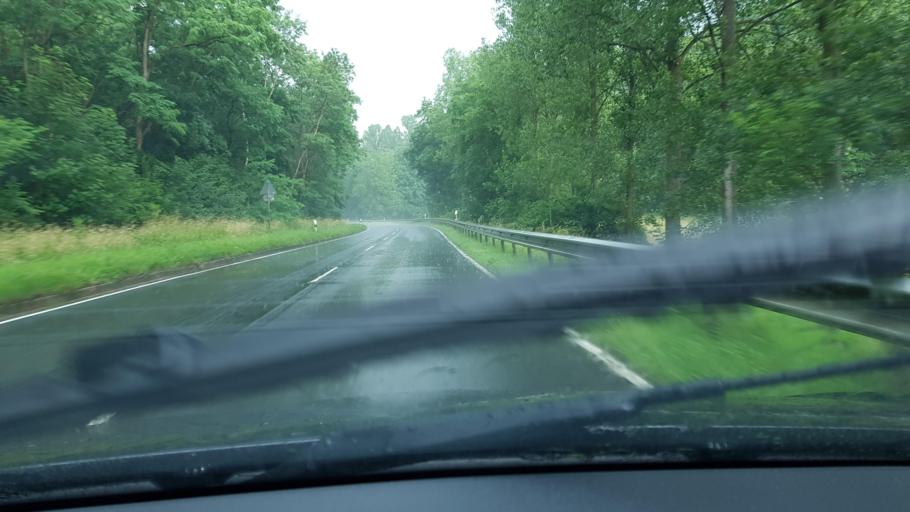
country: DE
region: Rheinland-Pfalz
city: Sinzig
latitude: 50.5303
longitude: 7.2525
